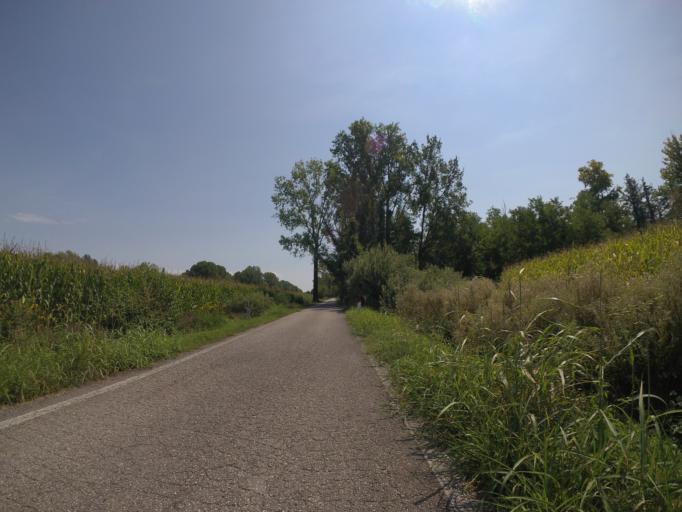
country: IT
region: Friuli Venezia Giulia
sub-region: Provincia di Udine
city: Codroipo
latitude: 45.9410
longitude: 12.9926
